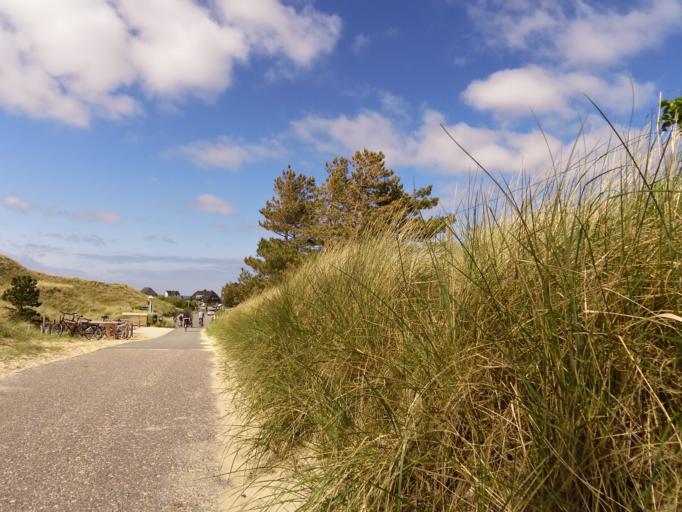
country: DE
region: Schleswig-Holstein
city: Wittdun
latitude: 54.6250
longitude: 8.3840
